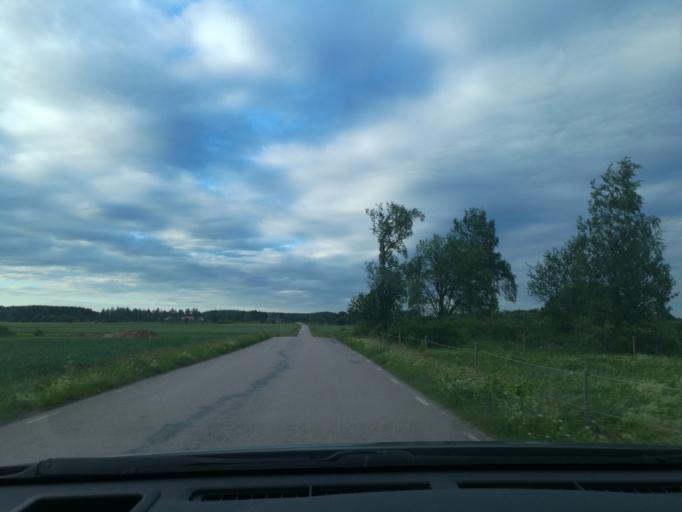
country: SE
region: Vaestmanland
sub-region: Hallstahammars Kommun
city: Kolback
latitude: 59.5369
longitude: 16.3008
